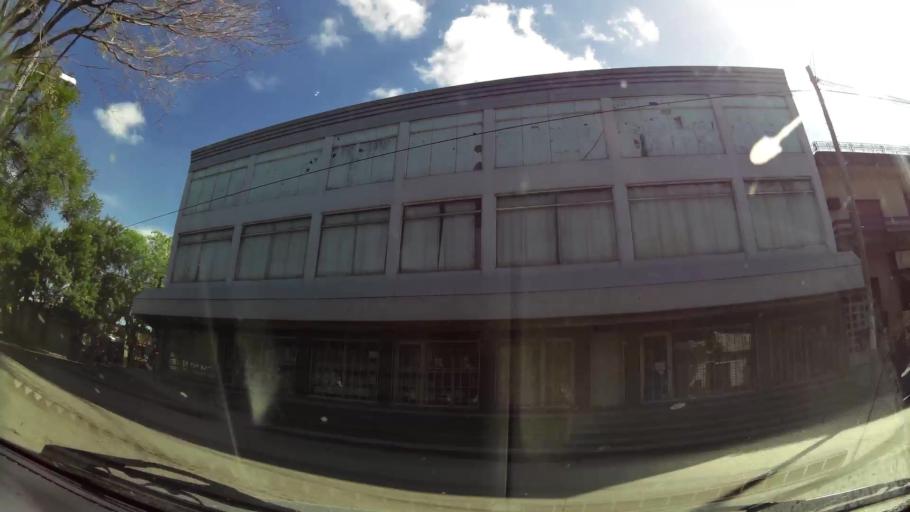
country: AR
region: Buenos Aires
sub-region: Partido de Quilmes
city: Quilmes
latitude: -34.8012
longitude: -58.2553
